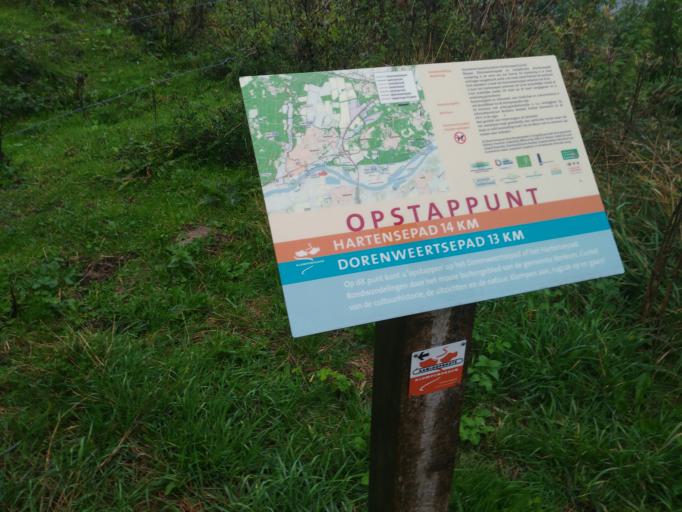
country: NL
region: Gelderland
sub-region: Gemeente Renkum
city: Renkum
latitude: 51.9699
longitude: 5.7350
